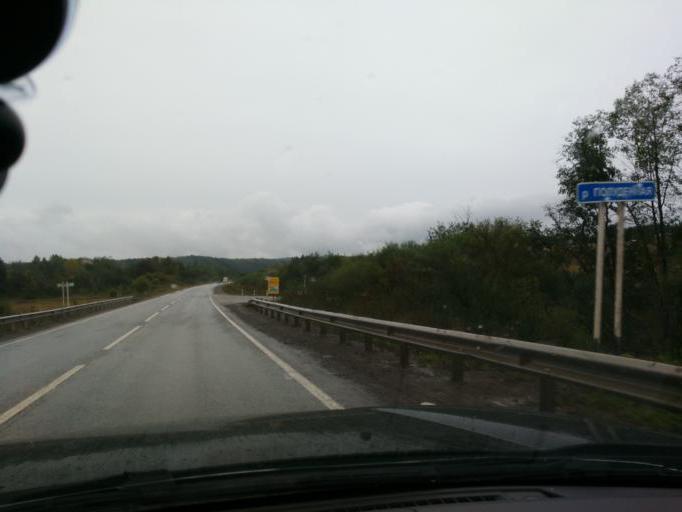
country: RU
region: Perm
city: Yugo-Kamskiy
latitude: 57.7120
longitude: 55.6366
